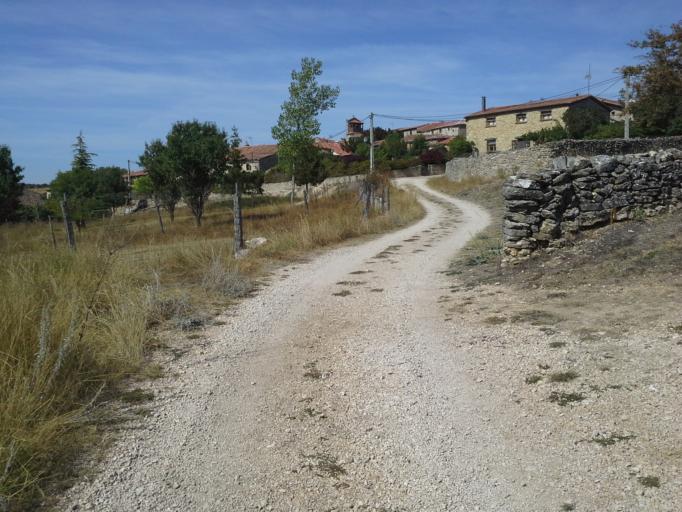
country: ES
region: Castille and Leon
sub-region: Provincia de Soria
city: Abejar
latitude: 41.7378
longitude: -2.7392
